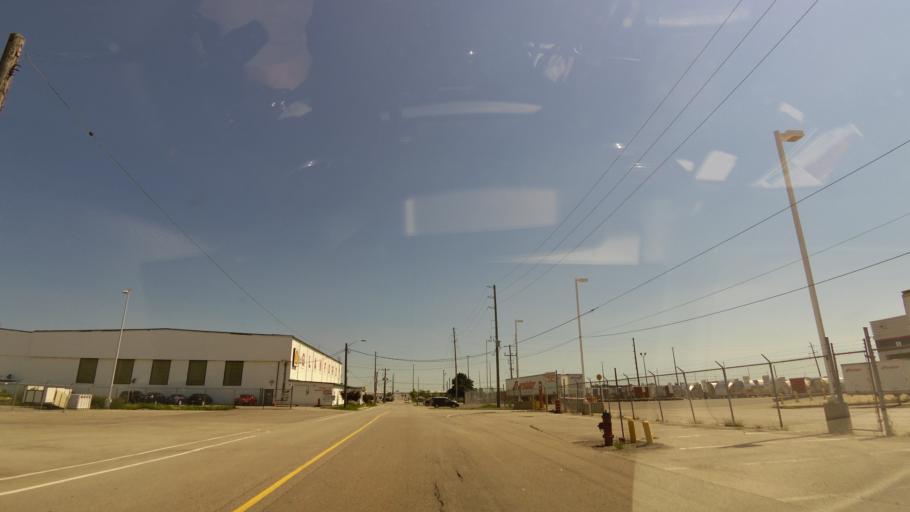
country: CA
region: Ontario
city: Ancaster
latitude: 43.1637
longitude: -79.9303
